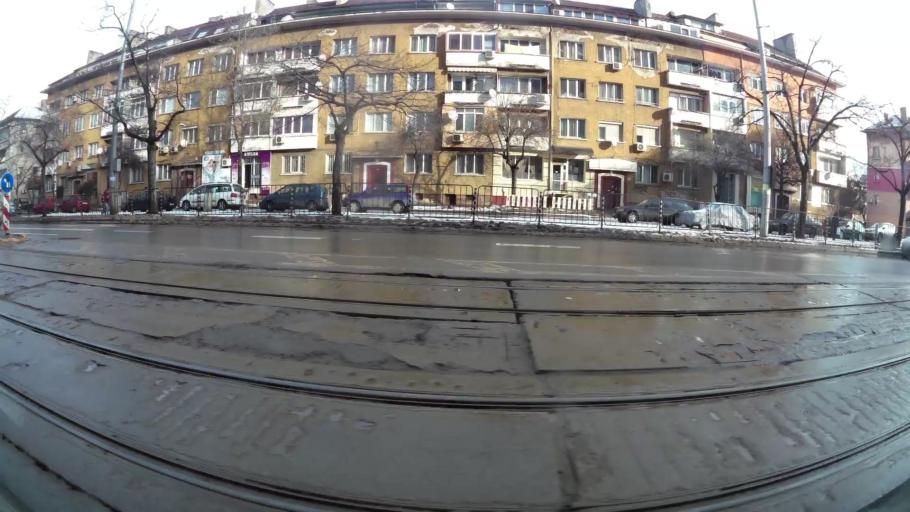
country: BG
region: Sofia-Capital
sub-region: Stolichna Obshtina
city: Sofia
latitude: 42.7009
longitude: 23.2929
